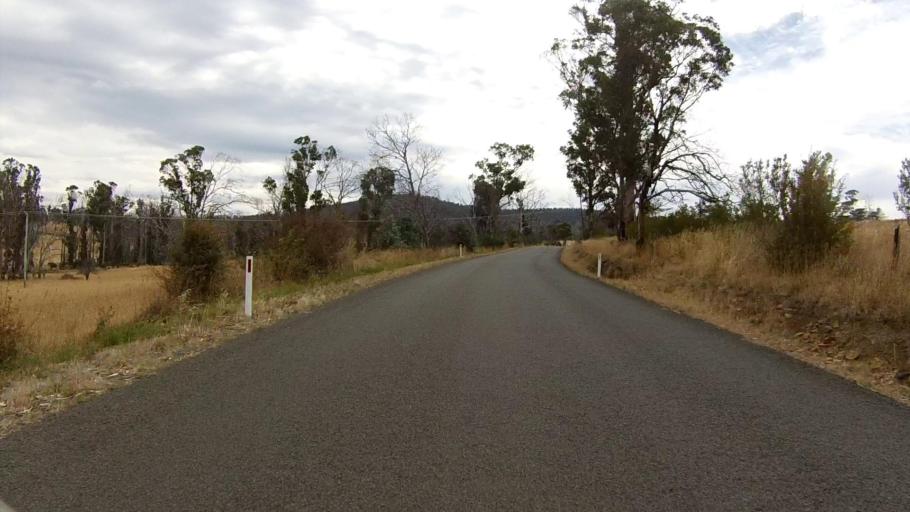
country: AU
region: Tasmania
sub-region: Sorell
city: Sorell
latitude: -42.8941
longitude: 147.7793
